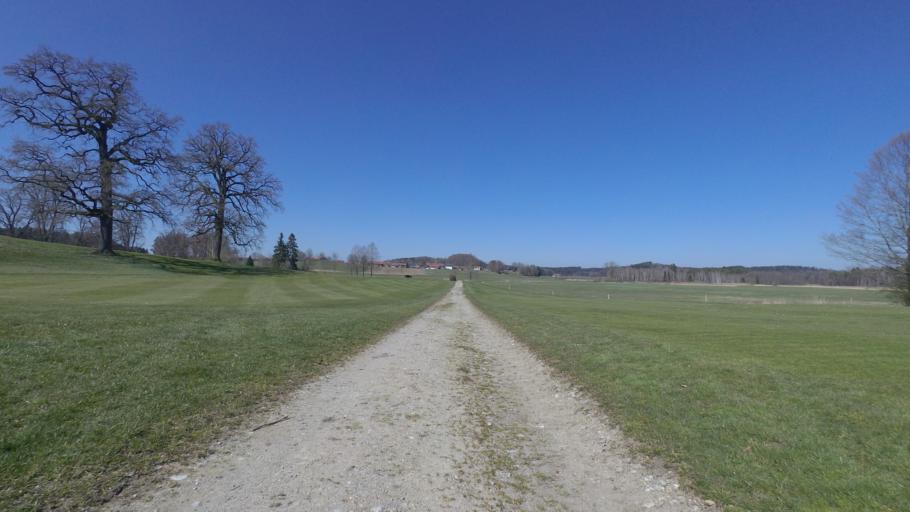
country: DE
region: Bavaria
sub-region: Upper Bavaria
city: Chieming
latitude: 47.9268
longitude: 12.5083
